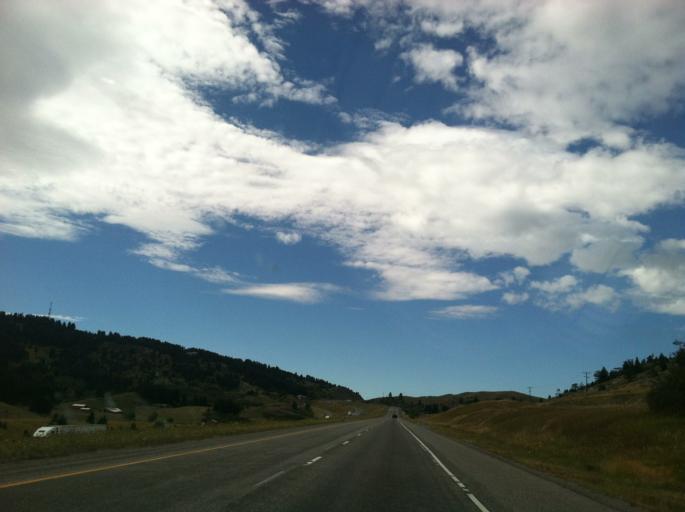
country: US
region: Montana
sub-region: Park County
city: Livingston
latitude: 45.6594
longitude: -110.7842
